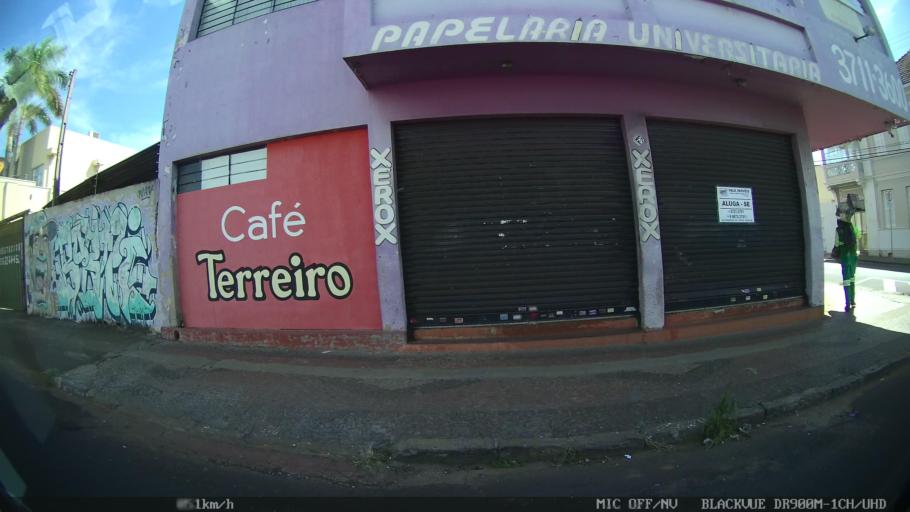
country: BR
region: Sao Paulo
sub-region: Franca
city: Franca
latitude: -20.5323
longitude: -47.4113
